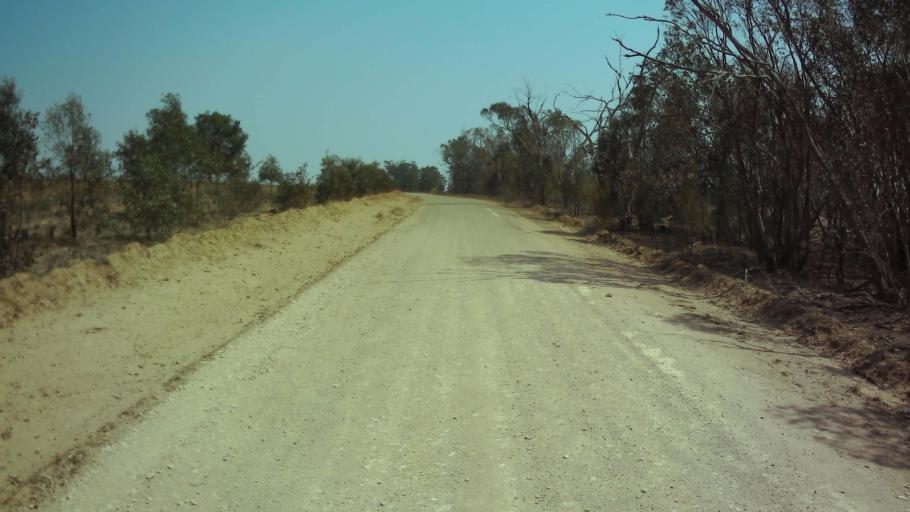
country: AU
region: New South Wales
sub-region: Weddin
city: Grenfell
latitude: -33.6580
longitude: 148.2744
